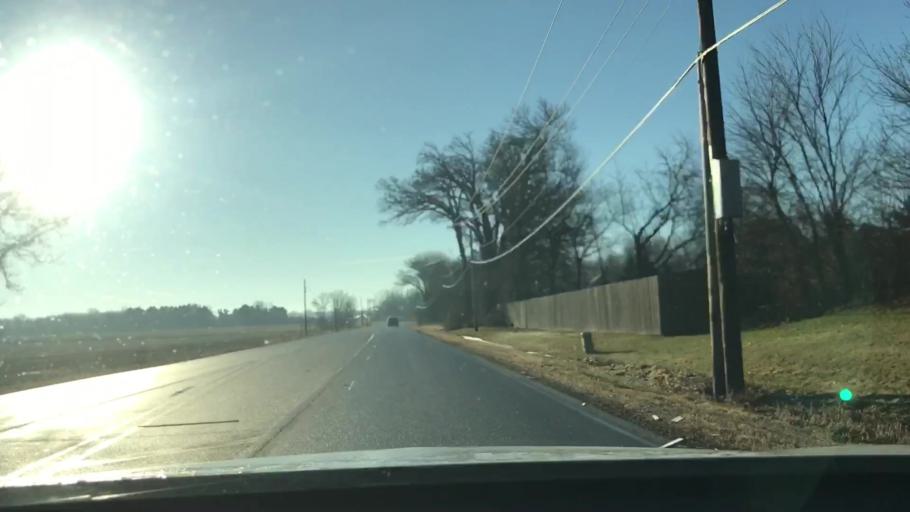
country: US
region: Illinois
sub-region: Kane County
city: Gilberts
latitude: 42.0948
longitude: -88.4006
